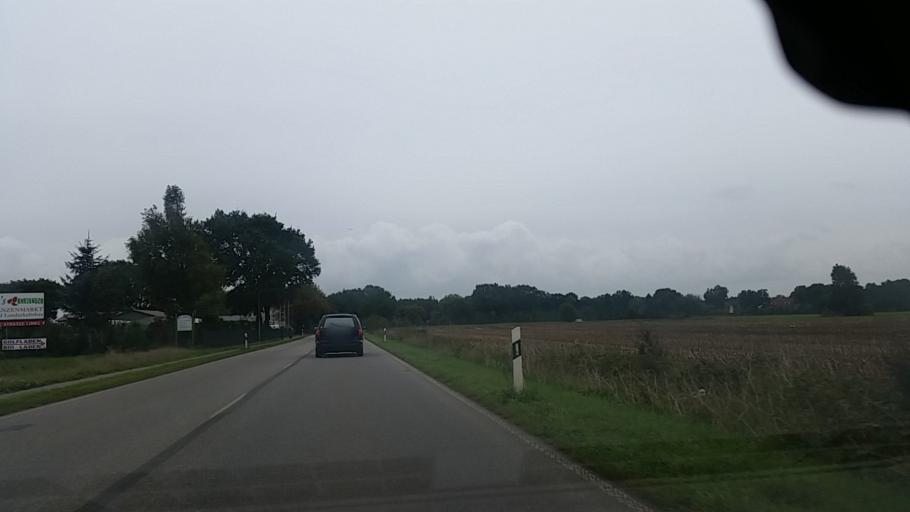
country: DE
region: Schleswig-Holstein
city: Kayhude
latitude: 53.7620
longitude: 10.1290
